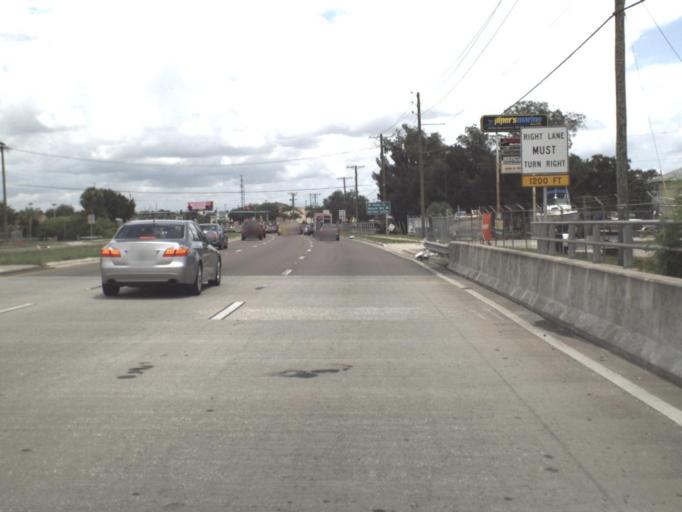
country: US
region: Florida
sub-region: Hillsborough County
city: Town 'n' Country
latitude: 27.9971
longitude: -82.5865
